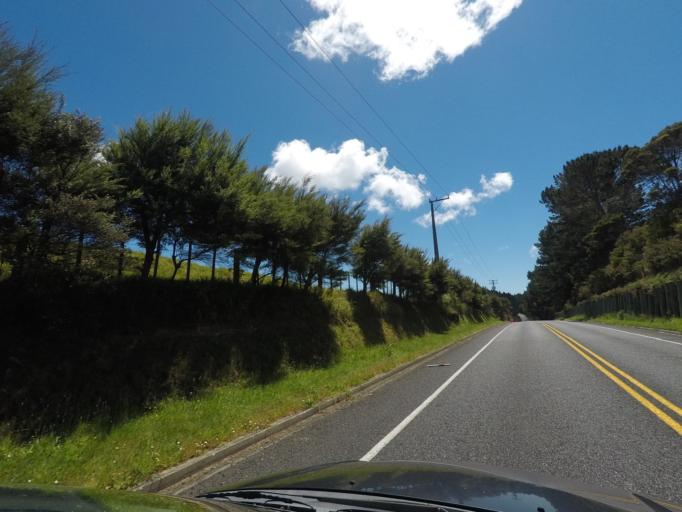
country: NZ
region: Auckland
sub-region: Auckland
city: Rothesay Bay
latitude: -36.7472
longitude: 174.6715
